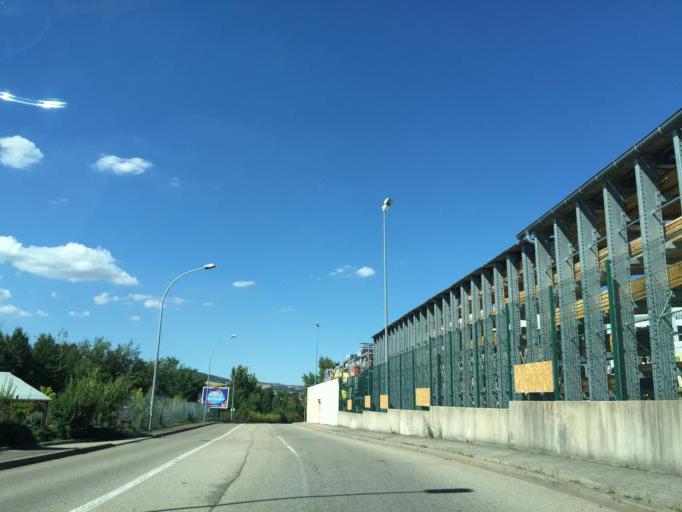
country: FR
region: Rhone-Alpes
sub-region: Departement de la Loire
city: Saint-Chamond
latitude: 45.4603
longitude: 4.4898
